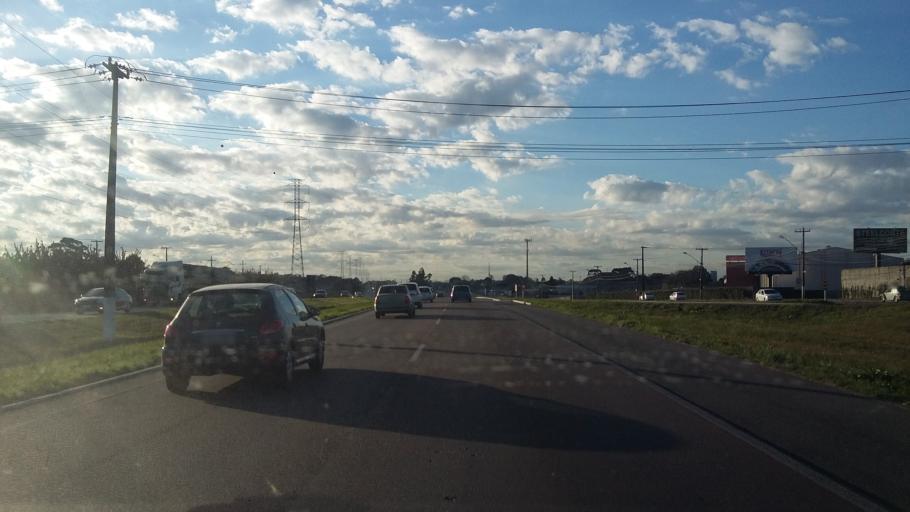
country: BR
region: Parana
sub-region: Curitiba
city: Curitiba
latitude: -25.4950
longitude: -49.3431
